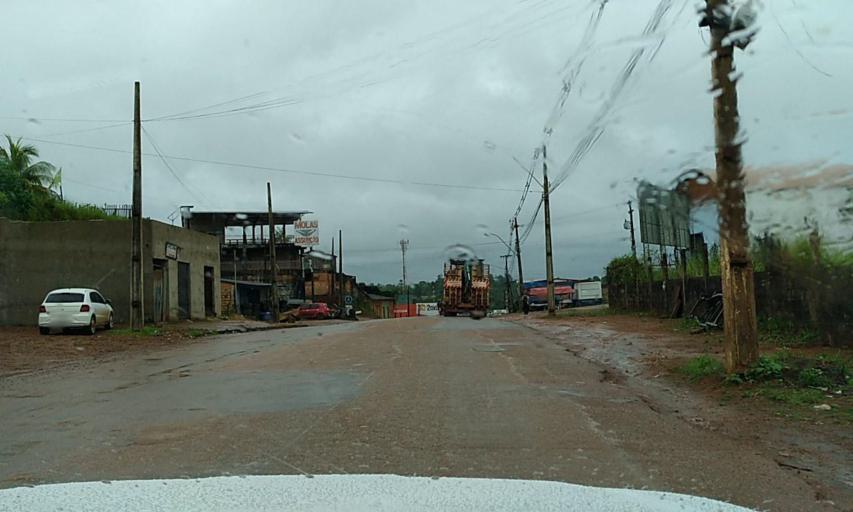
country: BR
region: Para
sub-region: Altamira
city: Altamira
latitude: -3.2140
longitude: -52.2350
